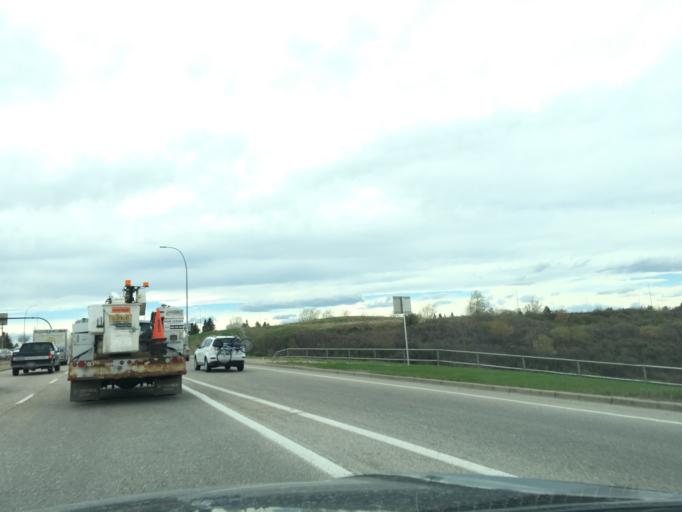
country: CA
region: Alberta
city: Calgary
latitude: 50.9670
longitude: -114.0354
